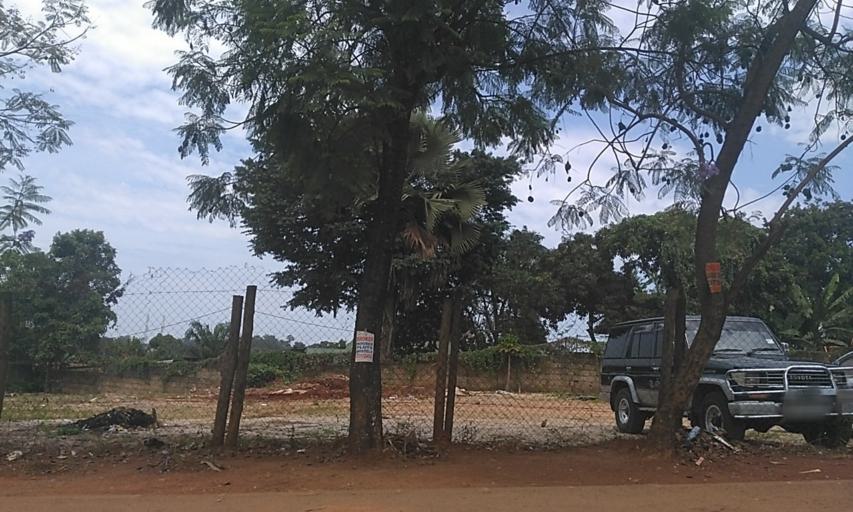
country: UG
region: Central Region
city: Kampala Central Division
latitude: 0.3058
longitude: 32.5497
